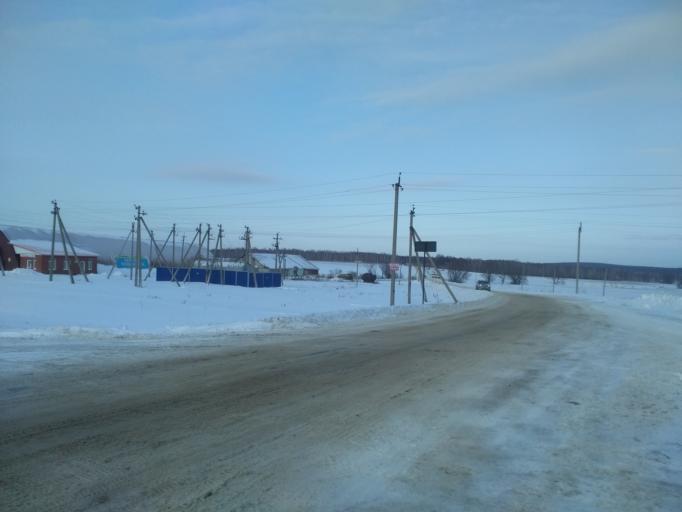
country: RU
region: Bashkortostan
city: Iglino
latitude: 54.7762
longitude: 56.5378
